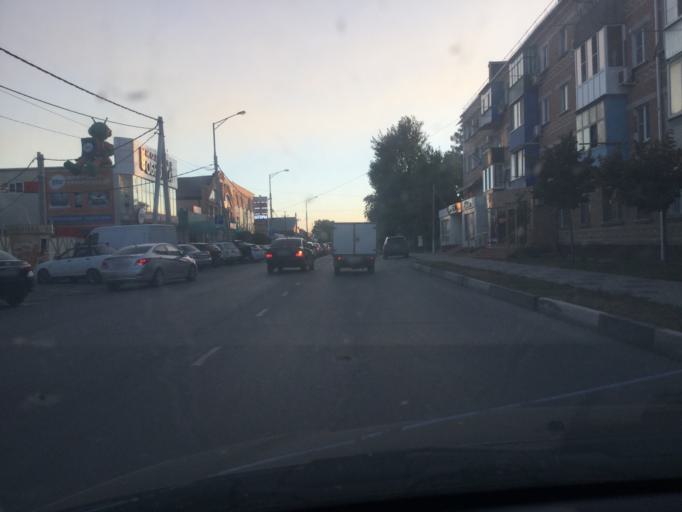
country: RU
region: Krasnodarskiy
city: Slavyansk-na-Kubani
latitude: 45.2547
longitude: 38.1191
